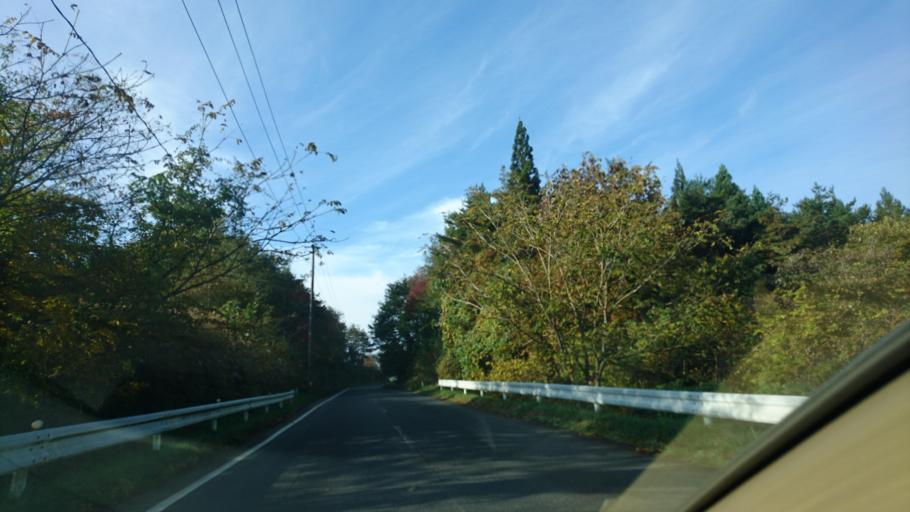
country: JP
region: Iwate
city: Ichinoseki
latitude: 39.0106
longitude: 141.3562
